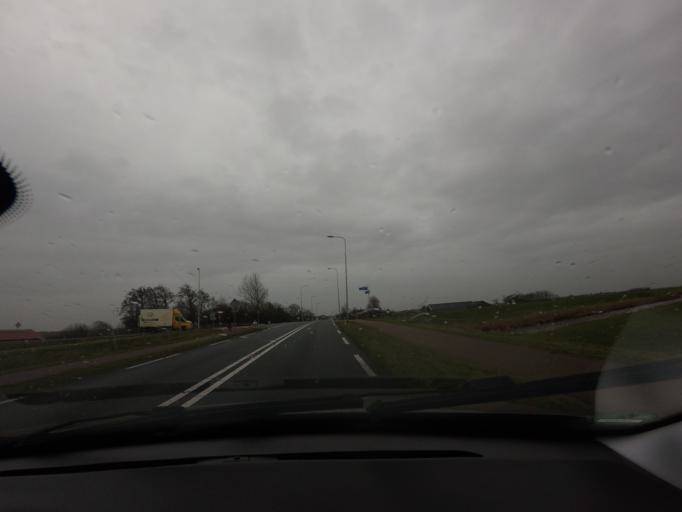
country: NL
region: North Holland
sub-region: Gemeente Texel
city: Den Burg
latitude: 53.0305
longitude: 4.8036
